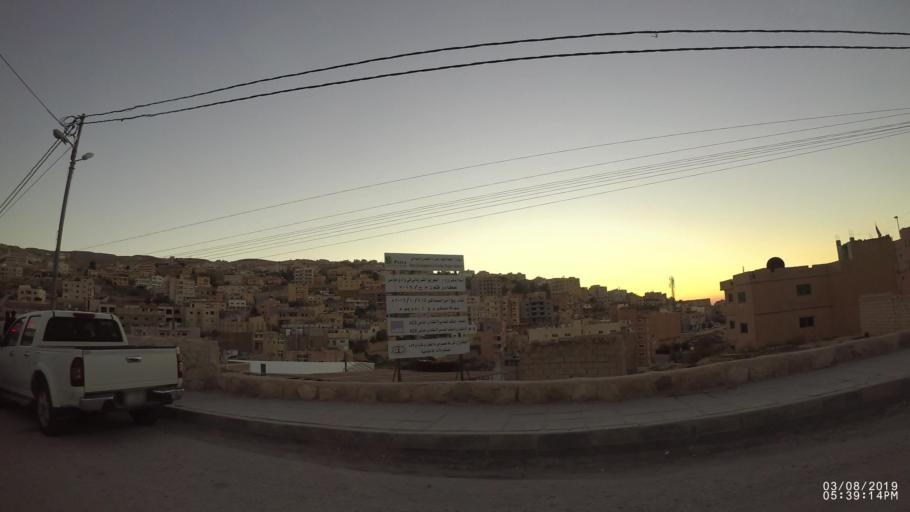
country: JO
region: Ma'an
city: Petra
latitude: 30.3194
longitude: 35.4796
